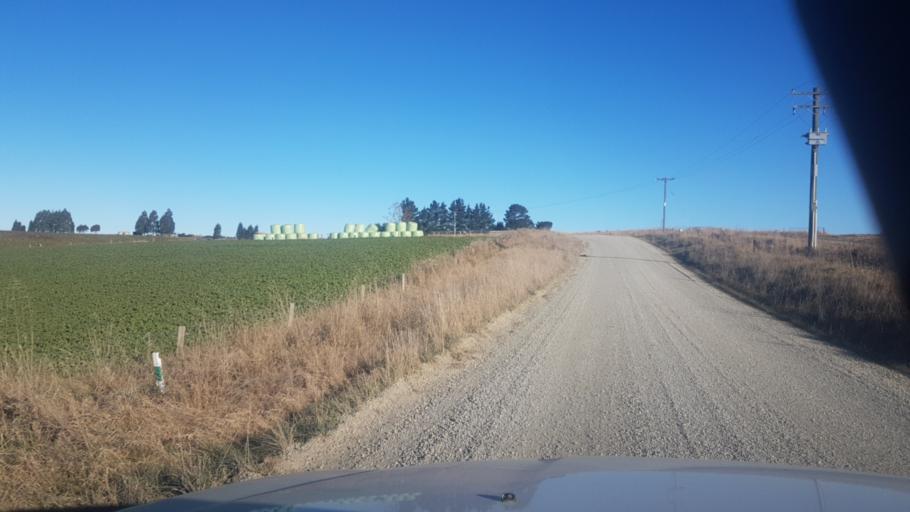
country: NZ
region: Canterbury
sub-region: Timaru District
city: Pleasant Point
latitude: -44.3554
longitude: 171.0696
